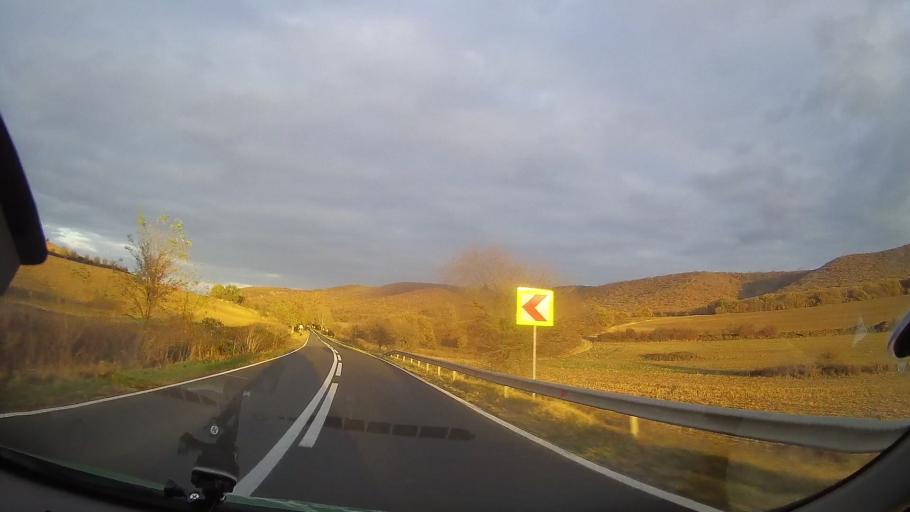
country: RO
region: Tulcea
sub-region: Comuna Ciucurova
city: Ciucurova
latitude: 44.9466
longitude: 28.5011
